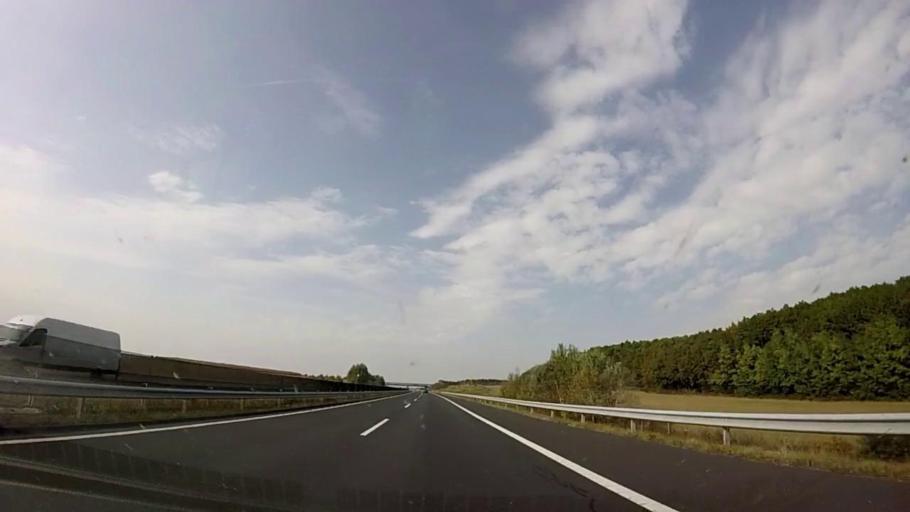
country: HU
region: Zala
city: Becsehely
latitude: 46.4495
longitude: 16.8443
